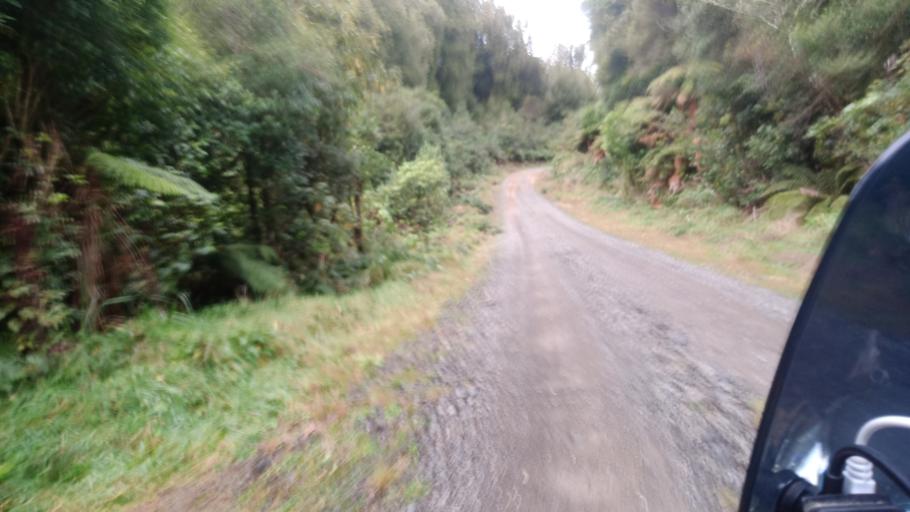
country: NZ
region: Bay of Plenty
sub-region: Whakatane District
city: Murupara
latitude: -38.6841
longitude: 176.6053
